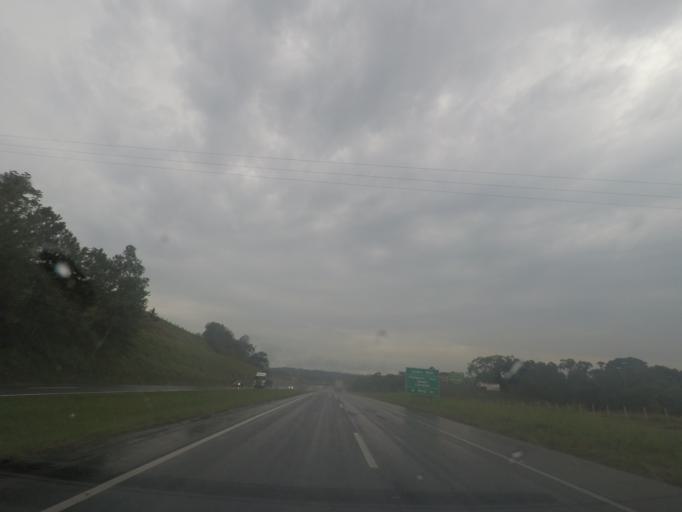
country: BR
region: Sao Paulo
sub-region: Pariquera-Acu
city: Pariquera Acu
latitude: -24.6403
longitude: -47.9145
